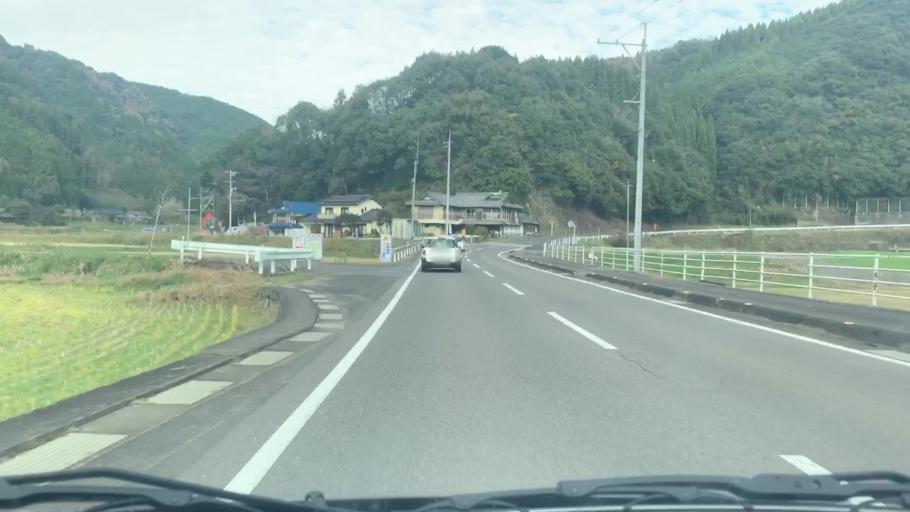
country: JP
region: Saga Prefecture
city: Imaricho-ko
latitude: 33.3262
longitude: 129.9683
